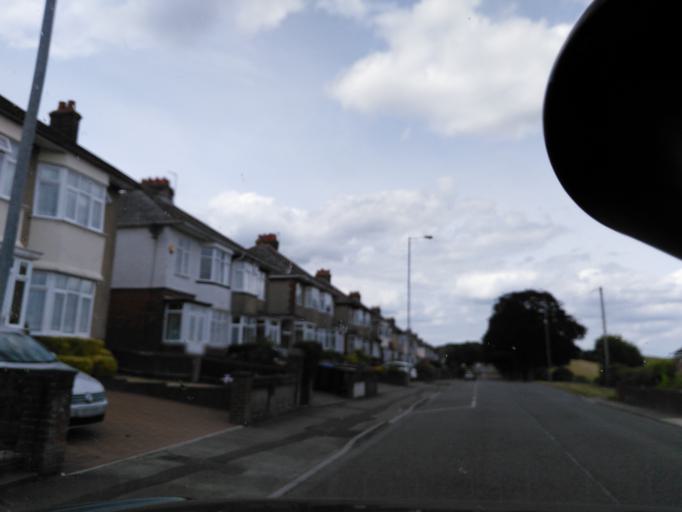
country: GB
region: England
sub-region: Wiltshire
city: Salisbury
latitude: 51.0857
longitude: -1.8225
